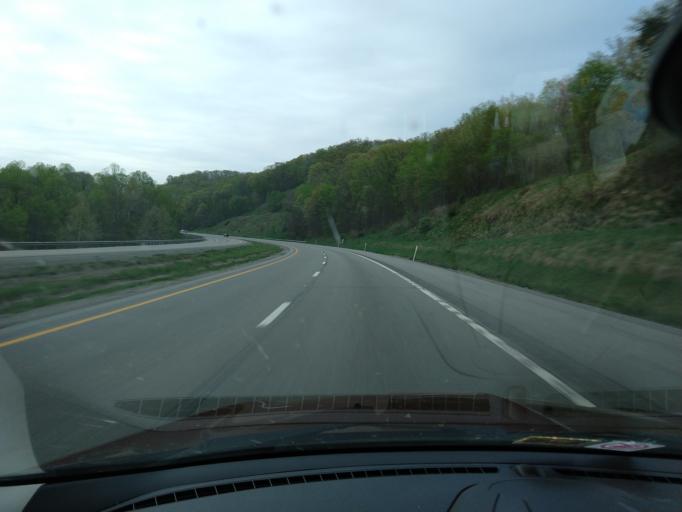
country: US
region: West Virginia
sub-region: Lewis County
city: Weston
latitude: 38.9213
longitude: -80.5512
